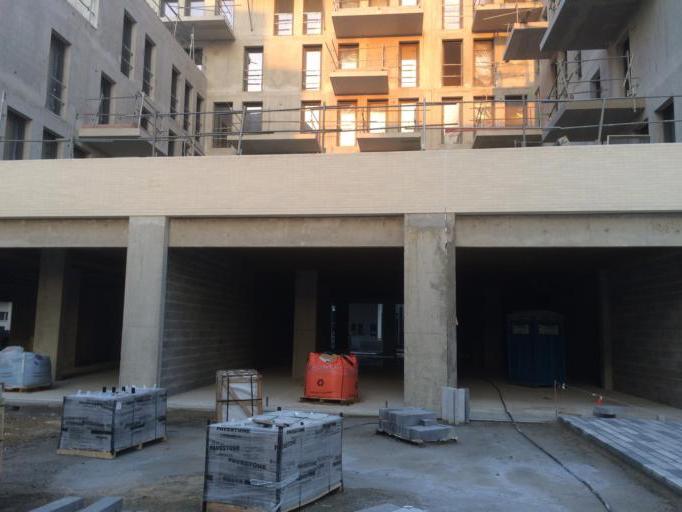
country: FR
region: Ile-de-France
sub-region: Departement de l'Essonne
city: Massy
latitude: 48.7329
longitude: 2.2890
